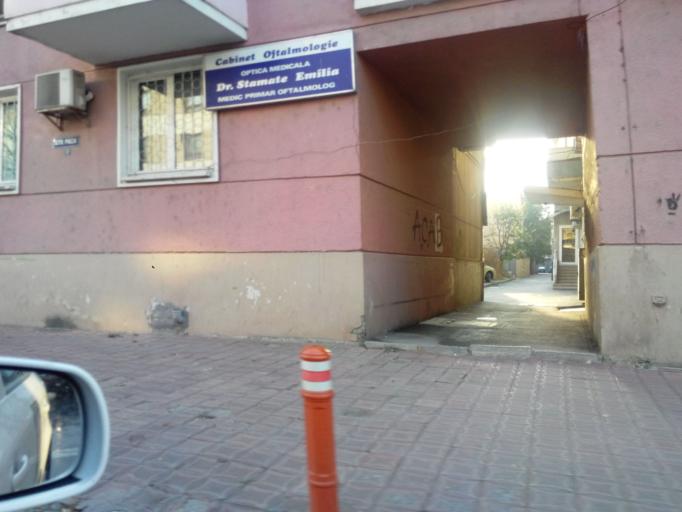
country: RO
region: Tulcea
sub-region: Municipiul Tulcea
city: Tulcea
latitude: 45.1794
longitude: 28.8047
